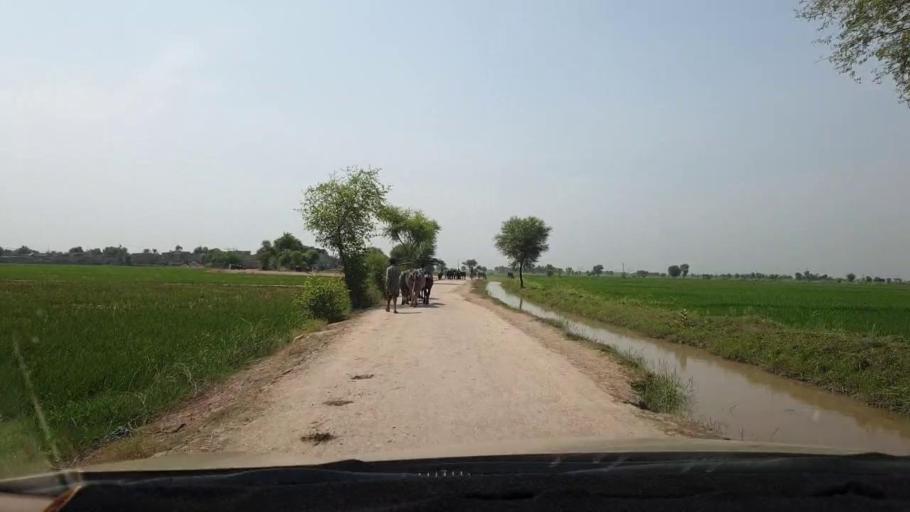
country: PK
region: Sindh
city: Naudero
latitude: 27.6512
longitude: 68.2597
